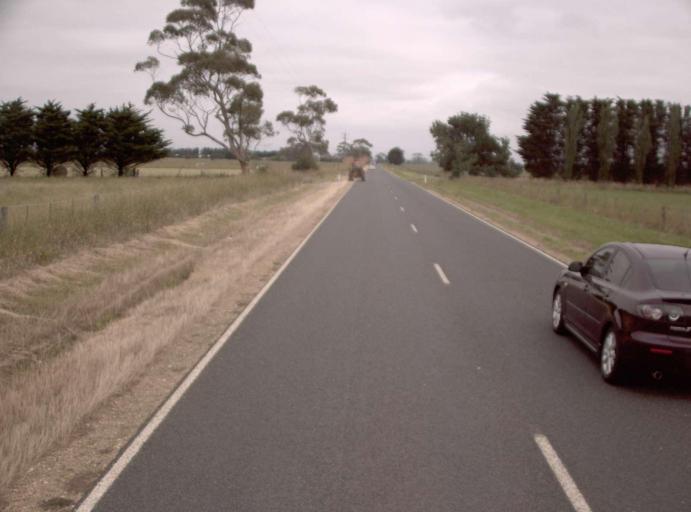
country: AU
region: Victoria
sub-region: Wellington
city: Sale
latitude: -38.0423
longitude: 146.9383
